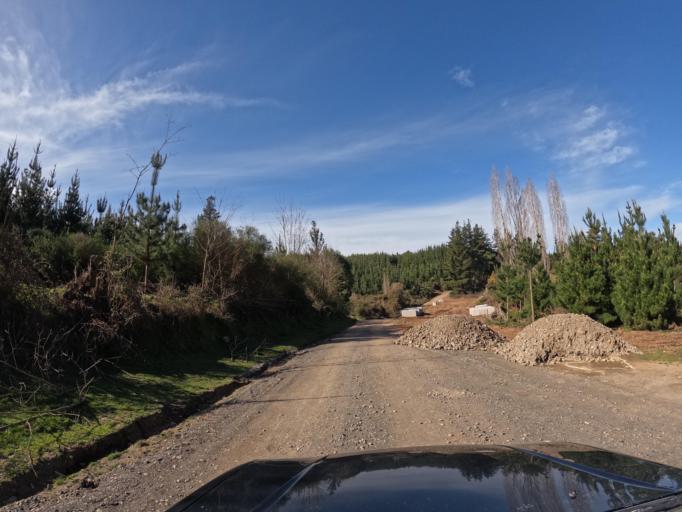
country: CL
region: Biobio
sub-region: Provincia de Biobio
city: La Laja
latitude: -37.0881
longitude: -72.7762
